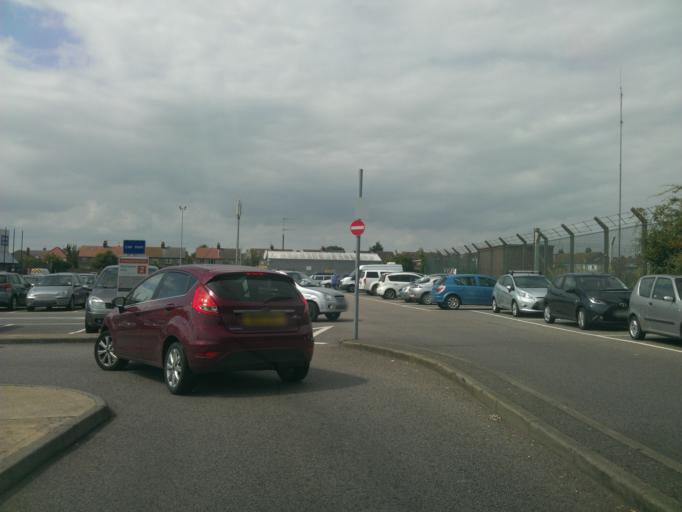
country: GB
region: England
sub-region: Essex
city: Clacton-on-Sea
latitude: 51.7906
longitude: 1.1473
